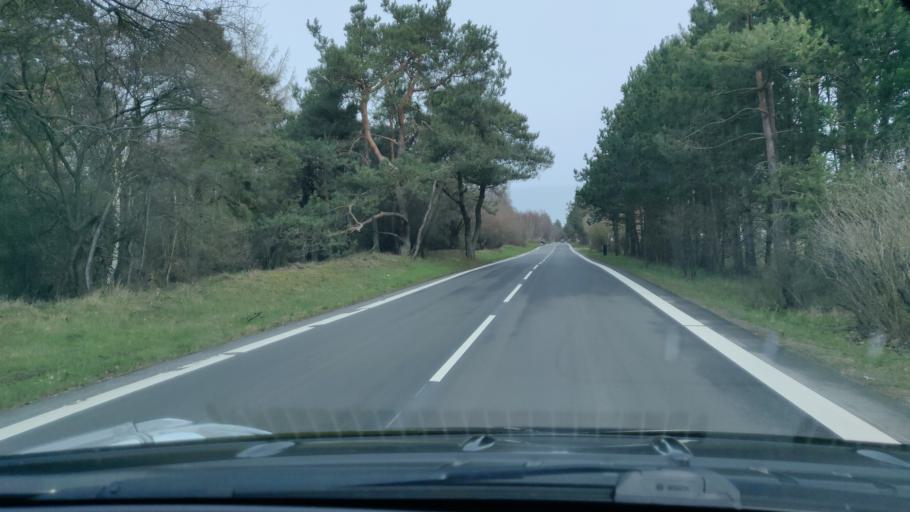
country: DK
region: Zealand
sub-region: Odsherred Kommune
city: Hojby
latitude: 55.8883
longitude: 11.5559
